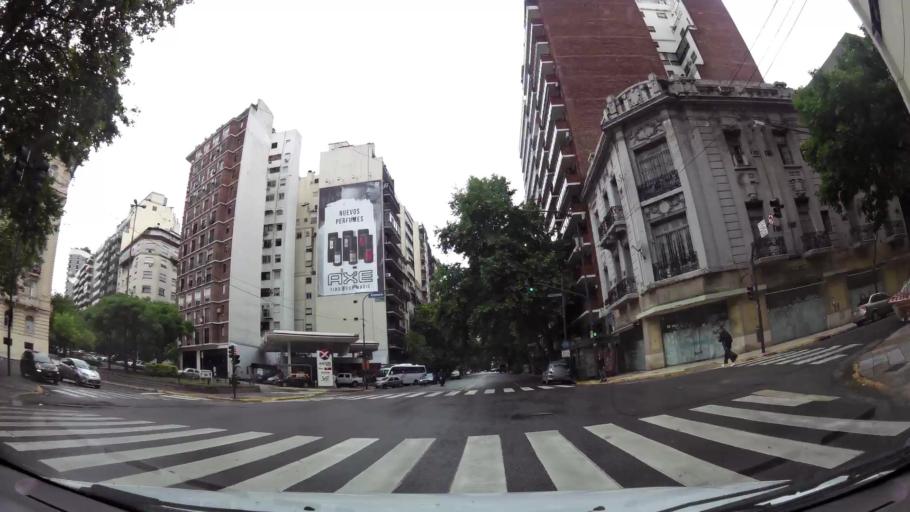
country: AR
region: Buenos Aires F.D.
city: Retiro
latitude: -34.5857
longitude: -58.3992
